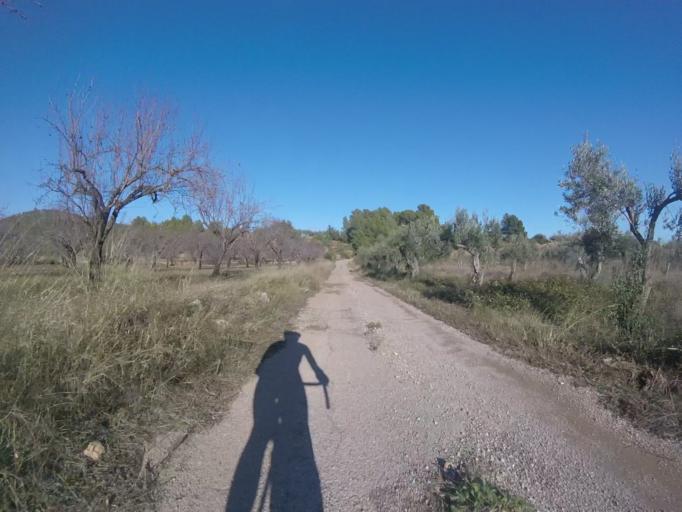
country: ES
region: Valencia
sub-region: Provincia de Castello
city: Sarratella
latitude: 40.2876
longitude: 0.0728
